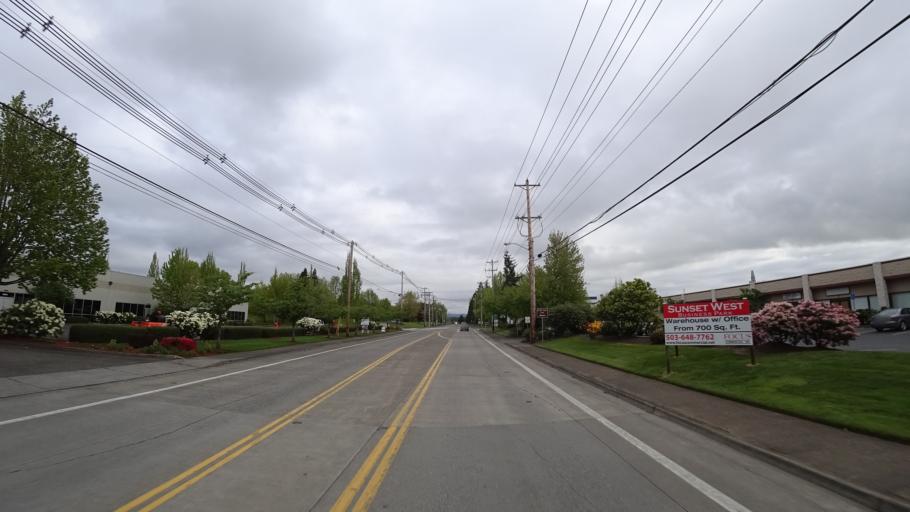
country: US
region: Oregon
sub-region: Washington County
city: Hillsboro
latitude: 45.5391
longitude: -122.9571
